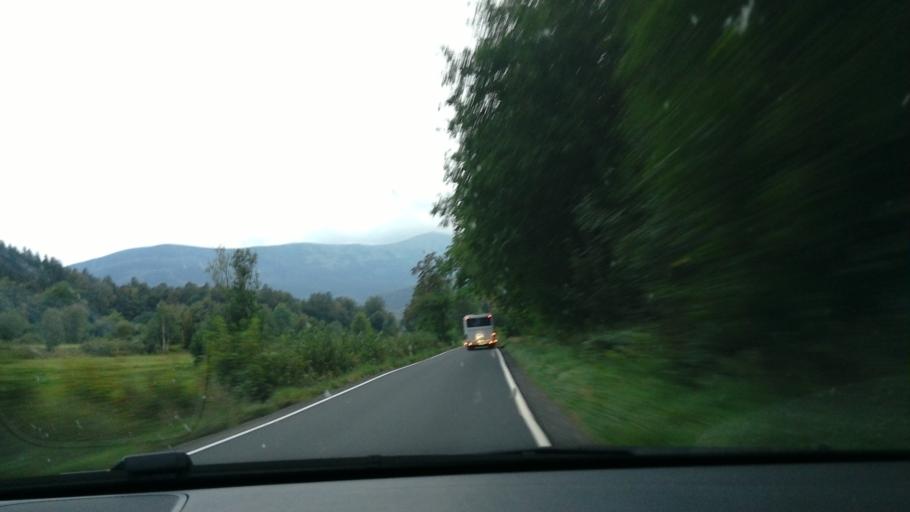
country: PL
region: Lower Silesian Voivodeship
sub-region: Powiat jeleniogorski
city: Karpacz
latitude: 50.7865
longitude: 15.7674
